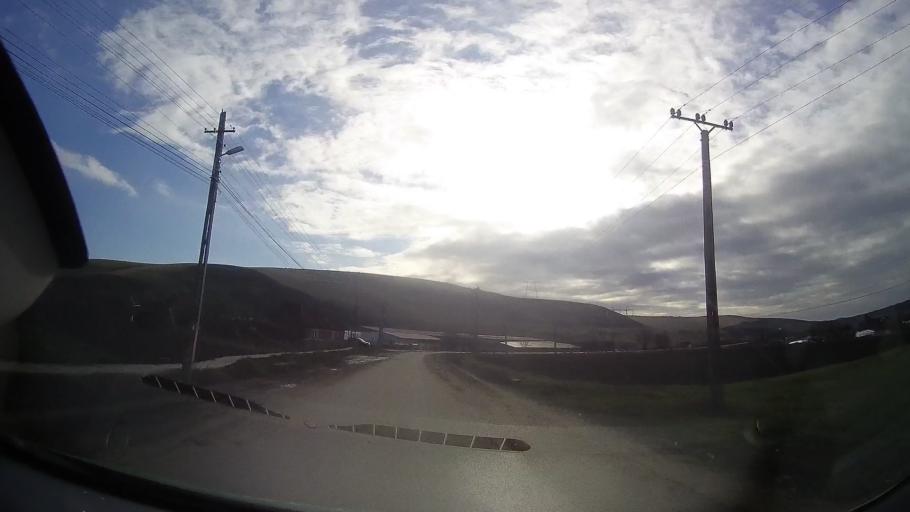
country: RO
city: Barza
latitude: 46.5502
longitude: 24.1288
